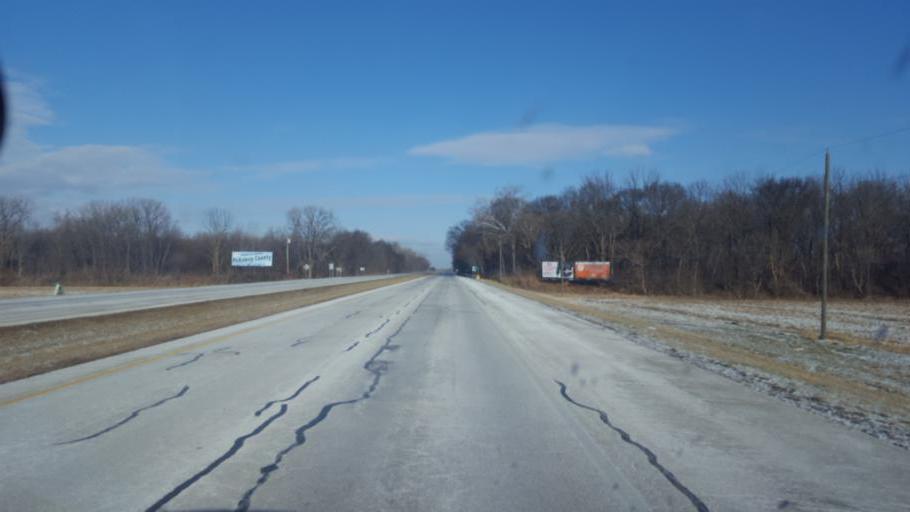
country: US
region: Ohio
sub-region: Pickaway County
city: Commercial Point
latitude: 39.8016
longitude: -82.9923
